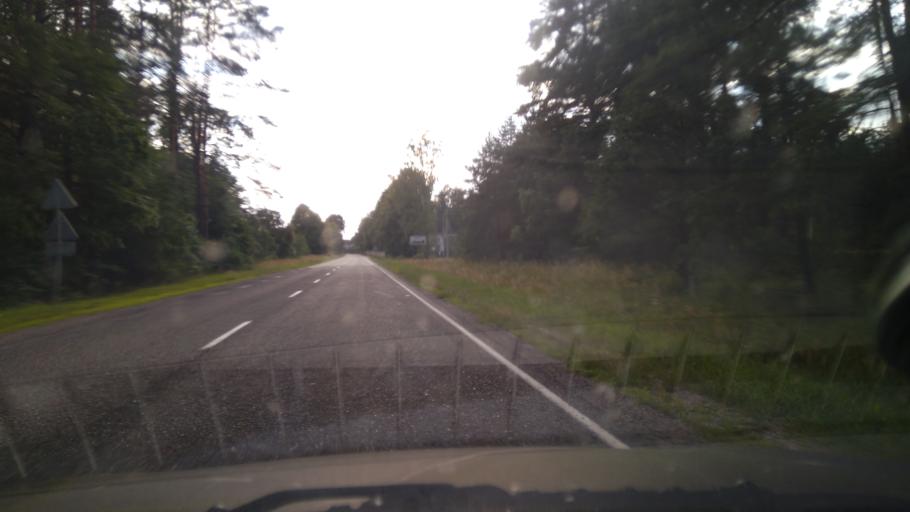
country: BY
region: Grodnenskaya
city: Masty
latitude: 53.3486
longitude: 24.6490
